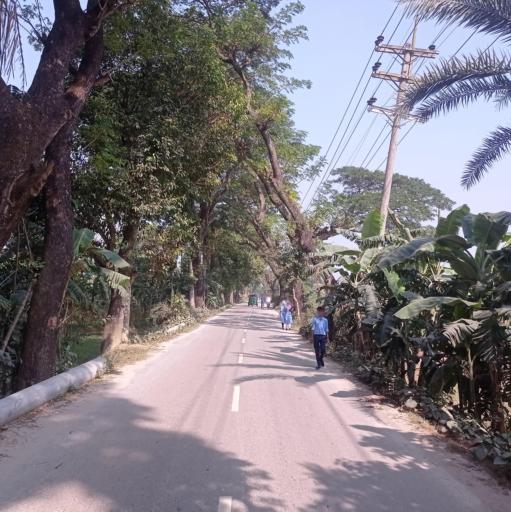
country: BD
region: Dhaka
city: Narsingdi
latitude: 24.0530
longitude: 90.6830
